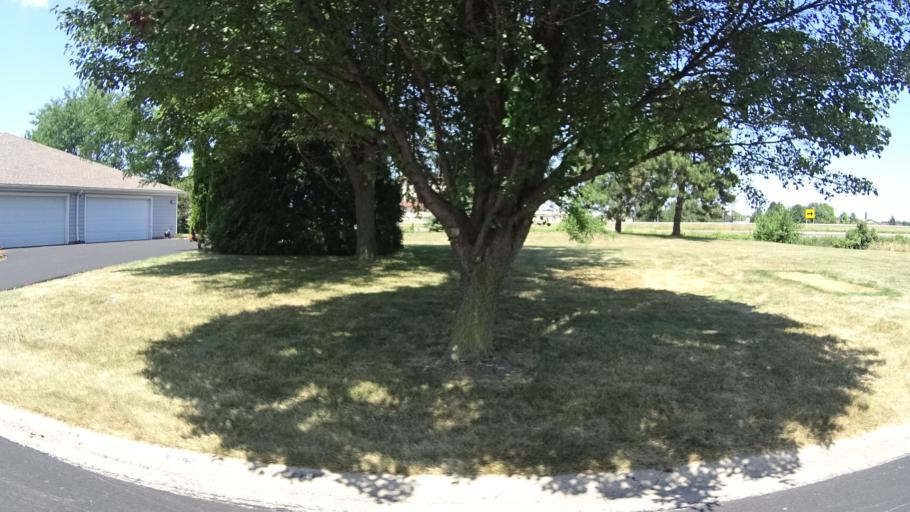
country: US
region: Ohio
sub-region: Erie County
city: Sandusky
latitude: 41.3988
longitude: -82.6588
